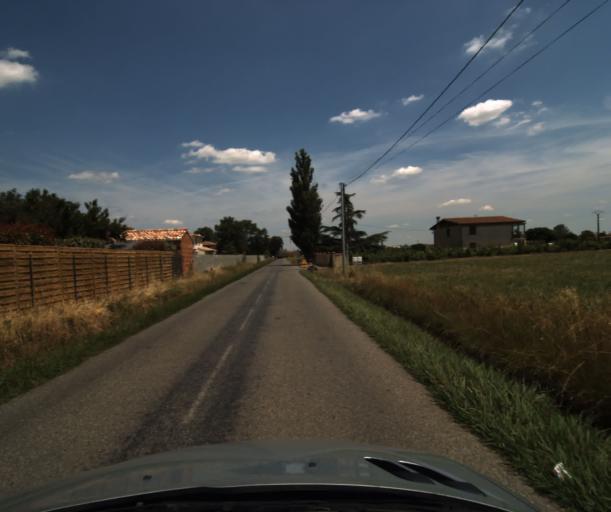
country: FR
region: Midi-Pyrenees
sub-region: Departement de la Haute-Garonne
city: Saint-Lys
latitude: 43.5070
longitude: 1.1782
